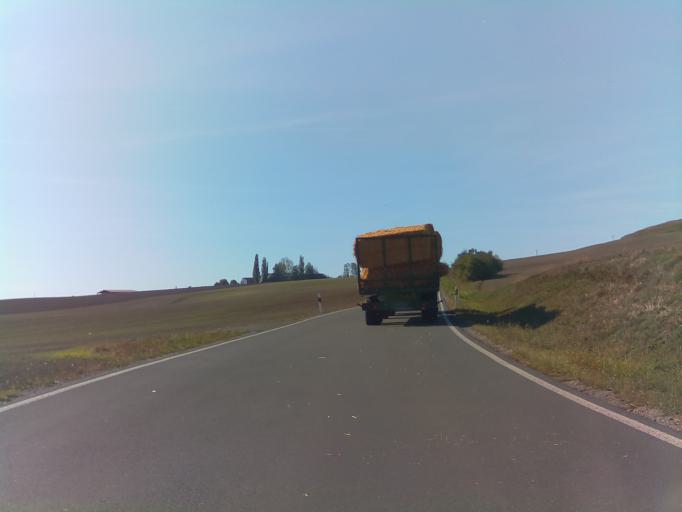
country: DE
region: Thuringia
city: Reinstadt
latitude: 50.7813
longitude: 11.3974
